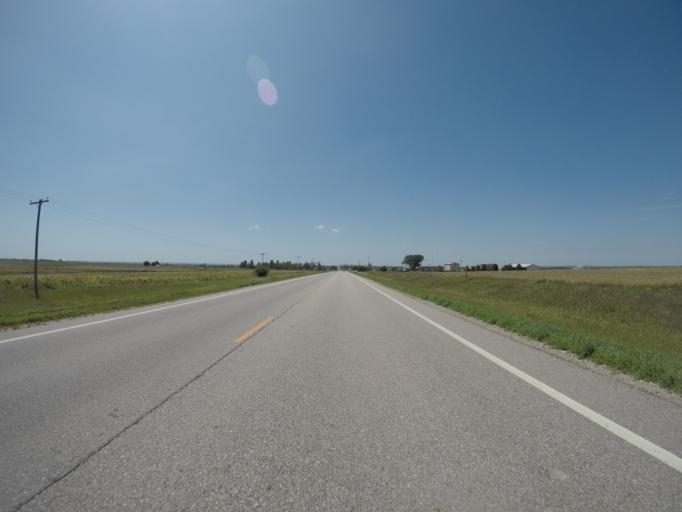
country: US
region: Kansas
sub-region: Osborne County
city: Osborne
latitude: 39.4579
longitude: -98.6947
